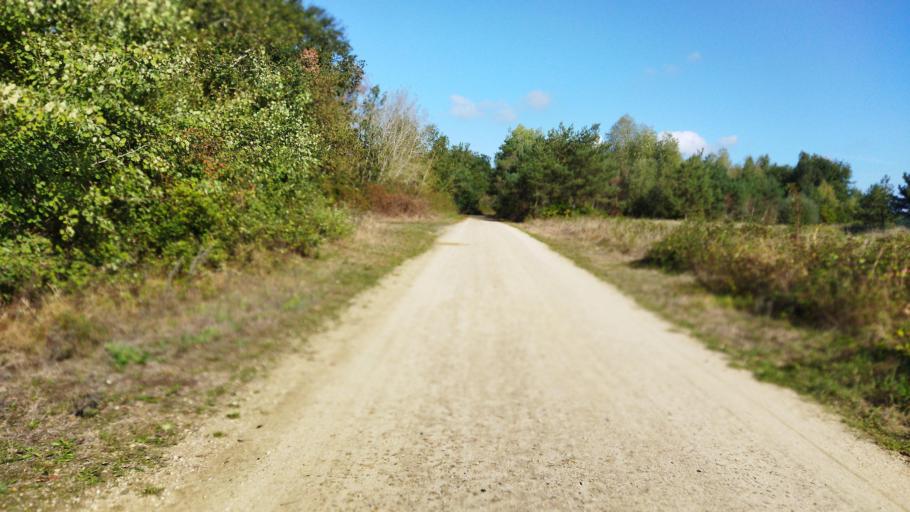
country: DE
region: Lower Saxony
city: Ohne
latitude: 52.2741
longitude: 7.3142
